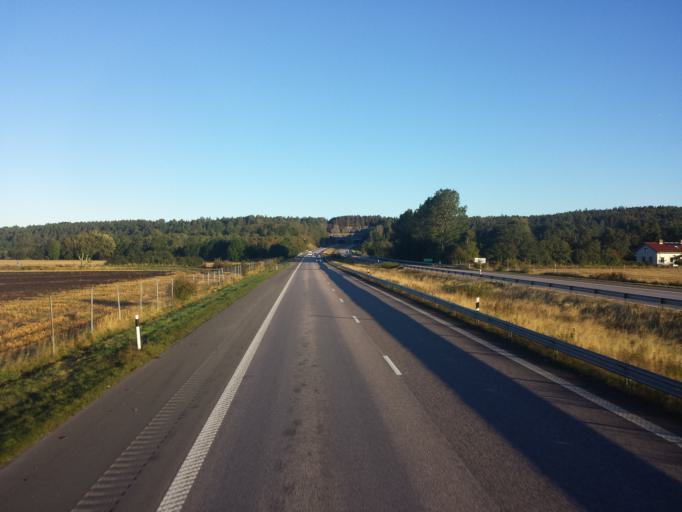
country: SE
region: Halland
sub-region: Varbergs Kommun
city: Veddige
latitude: 57.2270
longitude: 12.2302
